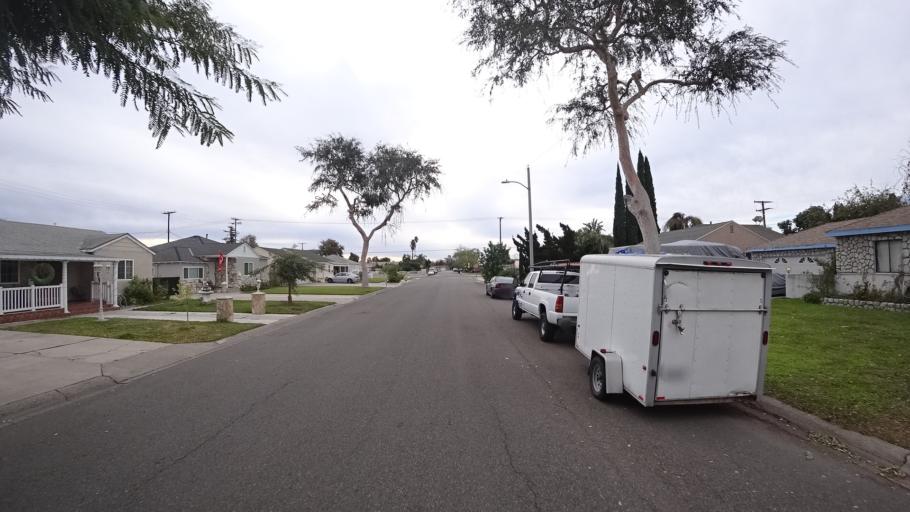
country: US
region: California
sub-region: Orange County
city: Garden Grove
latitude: 33.7715
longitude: -117.9330
